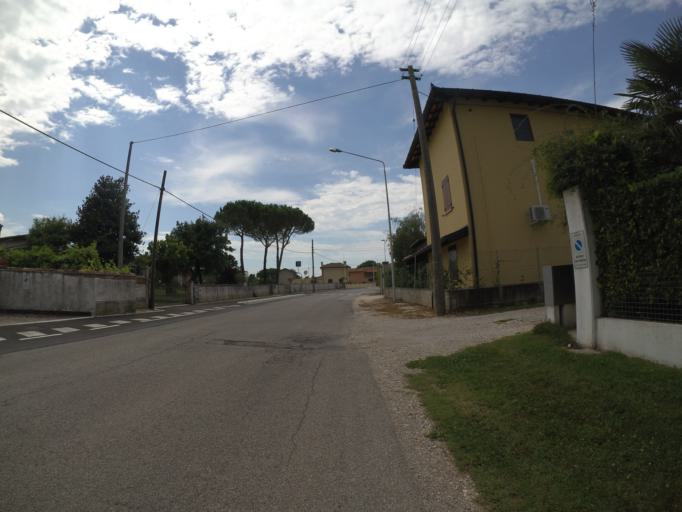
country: IT
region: Friuli Venezia Giulia
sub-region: Provincia di Udine
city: Talmassons
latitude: 45.9210
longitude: 13.1453
